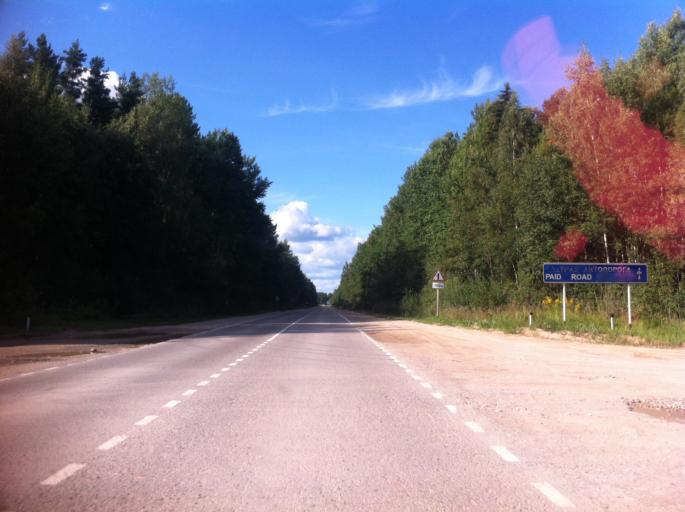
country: RU
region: Pskov
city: Pechory
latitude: 57.8099
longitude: 27.6535
